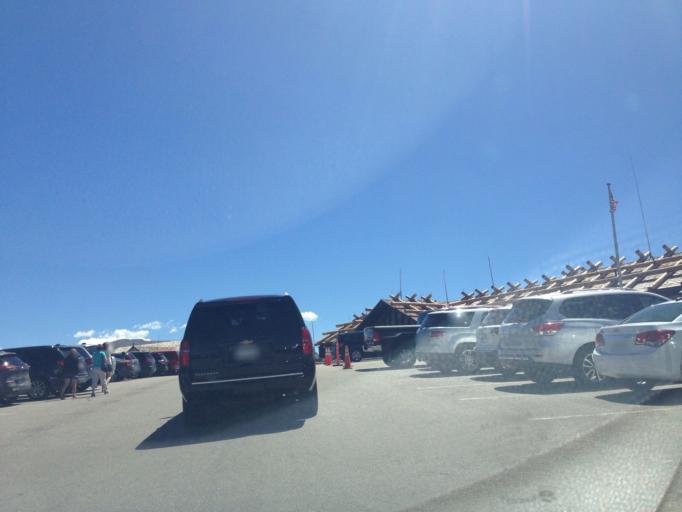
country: US
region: Colorado
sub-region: Larimer County
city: Estes Park
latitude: 40.4411
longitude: -105.7552
